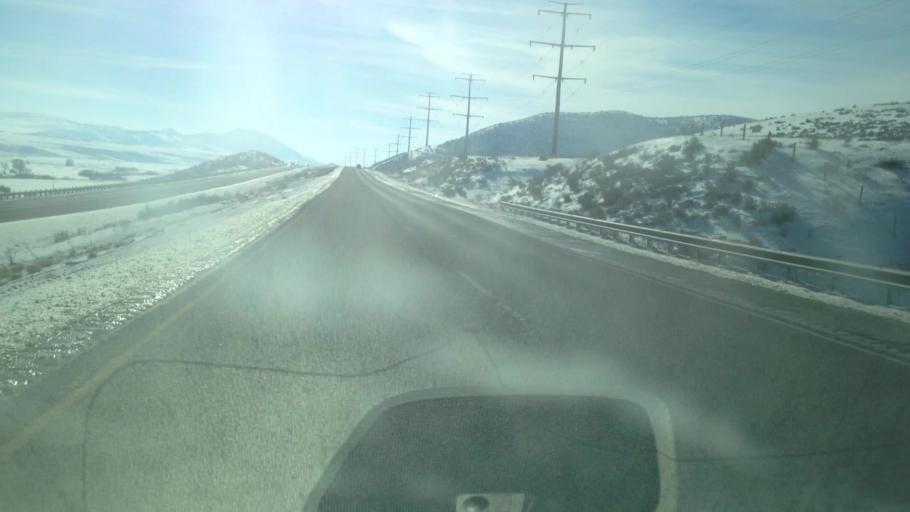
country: US
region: Idaho
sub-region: Oneida County
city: Malad City
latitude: 42.2723
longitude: -112.2134
